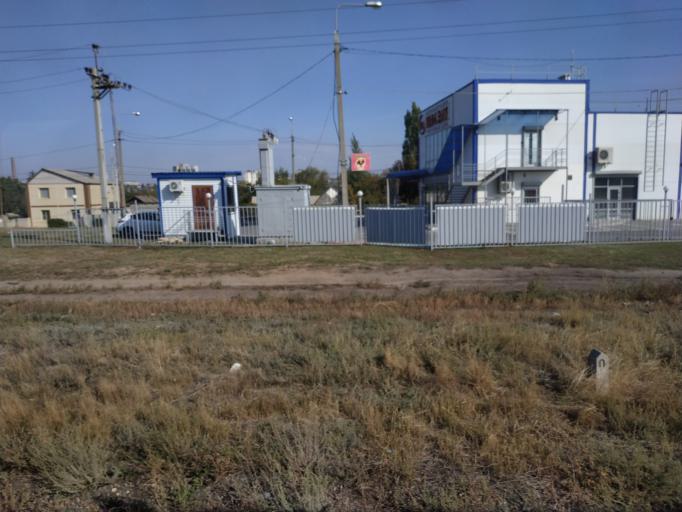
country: RU
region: Volgograd
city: Volgograd
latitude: 48.7503
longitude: 44.5319
